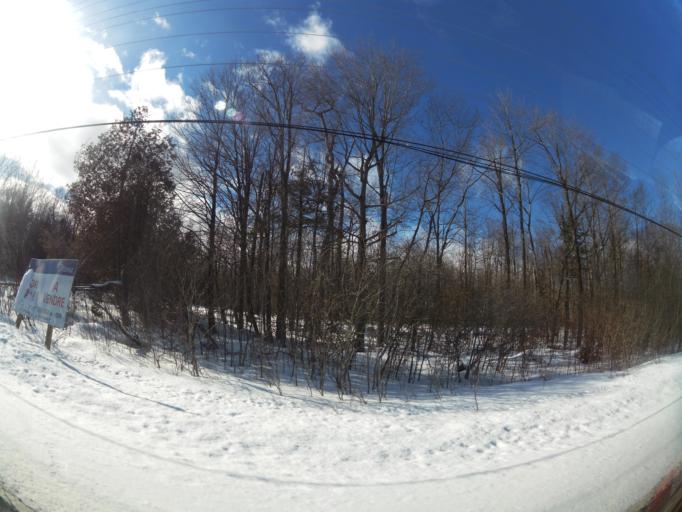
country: CA
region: Ontario
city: Ottawa
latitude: 45.2660
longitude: -75.5168
